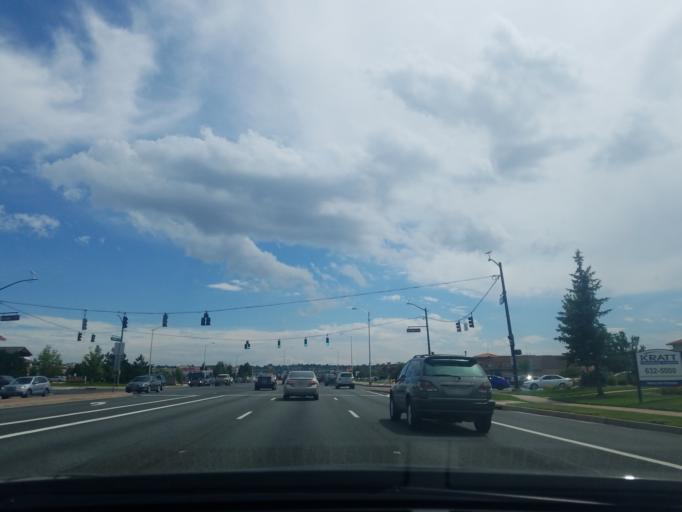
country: US
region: Colorado
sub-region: El Paso County
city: Air Force Academy
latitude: 38.9369
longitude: -104.7981
